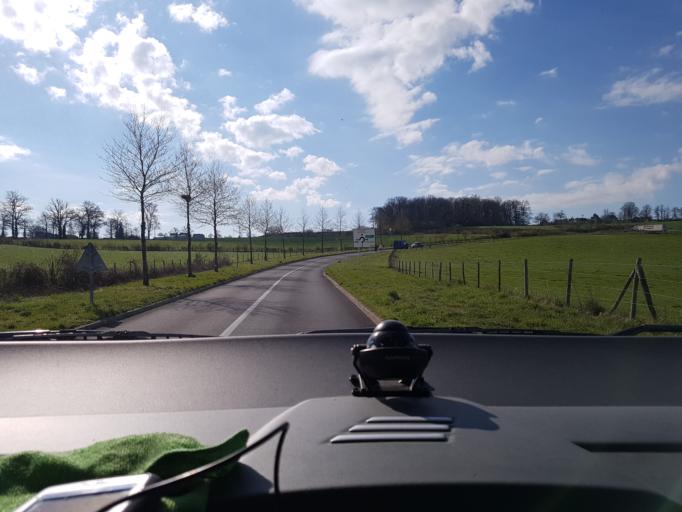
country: FR
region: Midi-Pyrenees
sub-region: Departement de l'Aveyron
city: Colombies
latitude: 44.4010
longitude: 2.3005
